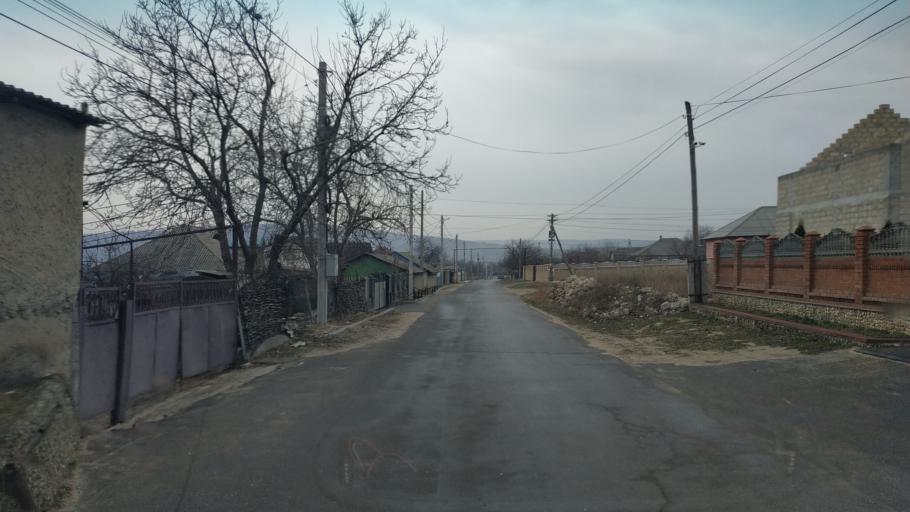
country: MD
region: Chisinau
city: Singera
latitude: 46.9197
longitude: 28.9593
